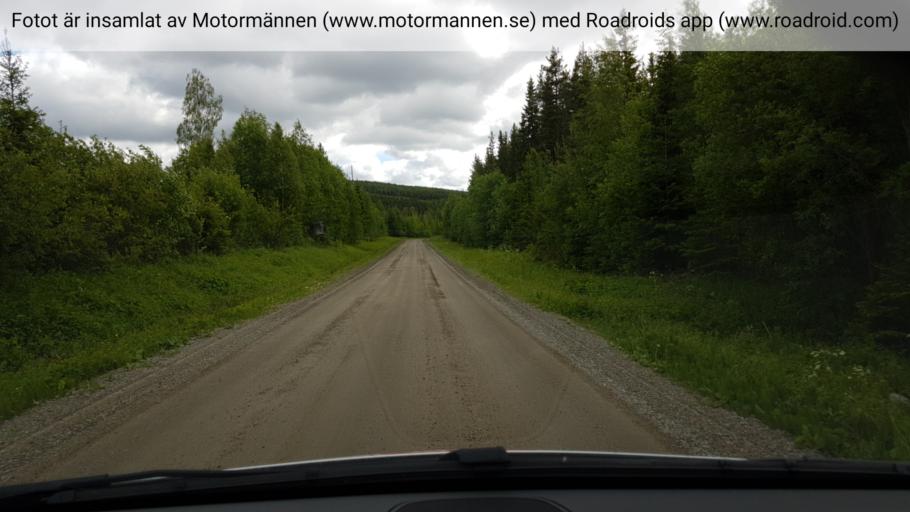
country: SE
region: Jaemtland
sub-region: Ragunda Kommun
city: Hammarstrand
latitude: 62.8750
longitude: 16.0578
